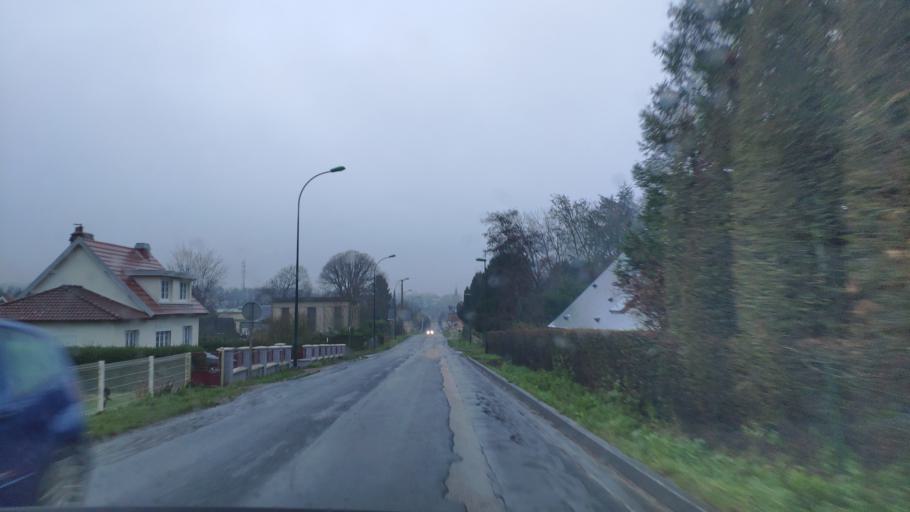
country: FR
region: Haute-Normandie
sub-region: Departement de la Seine-Maritime
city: Doudeville
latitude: 49.7196
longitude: 0.7710
